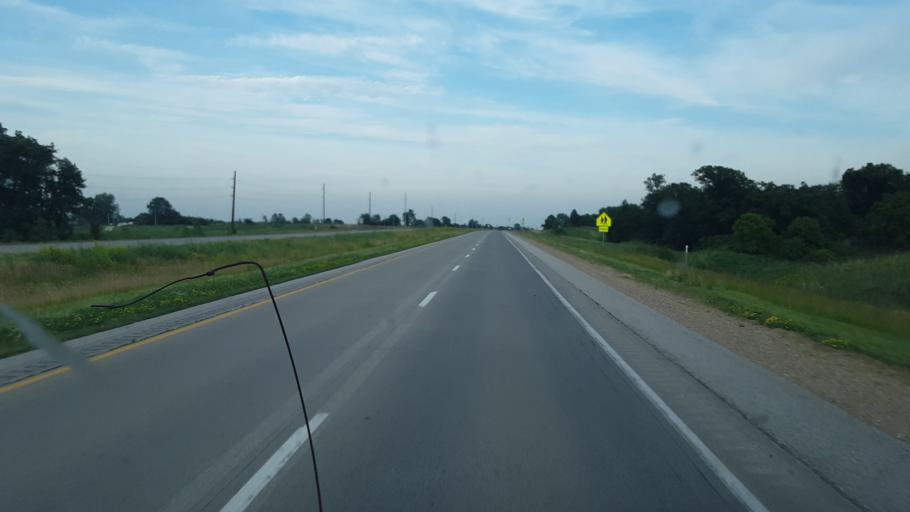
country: US
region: Iowa
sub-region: Tama County
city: Toledo
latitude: 41.9978
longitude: -92.6463
